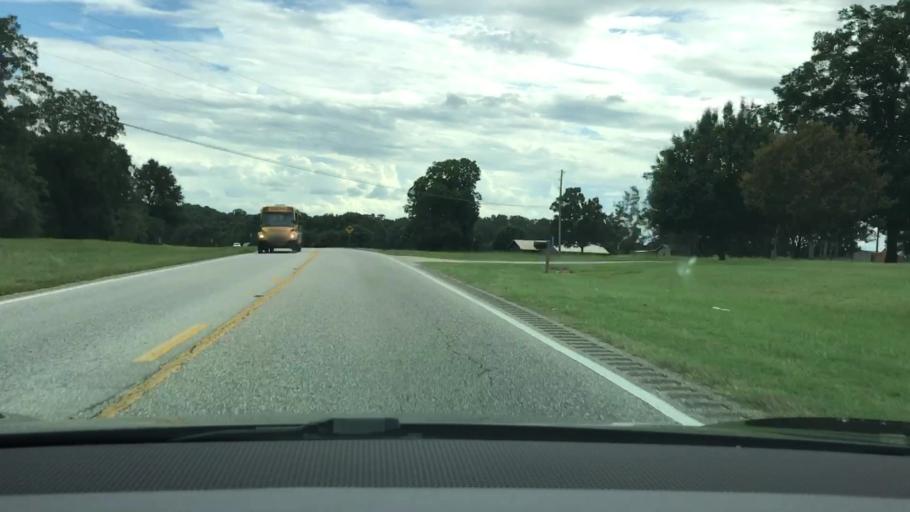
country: US
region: Alabama
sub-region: Pike County
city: Troy
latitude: 31.7224
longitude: -85.9597
